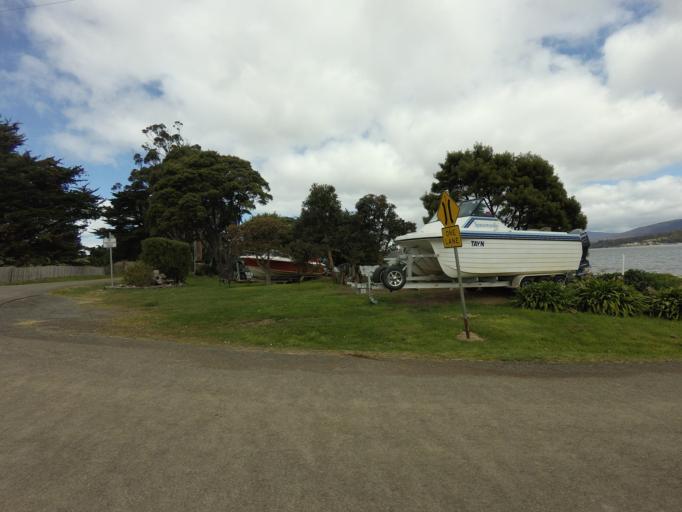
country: AU
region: Tasmania
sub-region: Huon Valley
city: Geeveston
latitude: -43.4357
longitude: 146.9830
